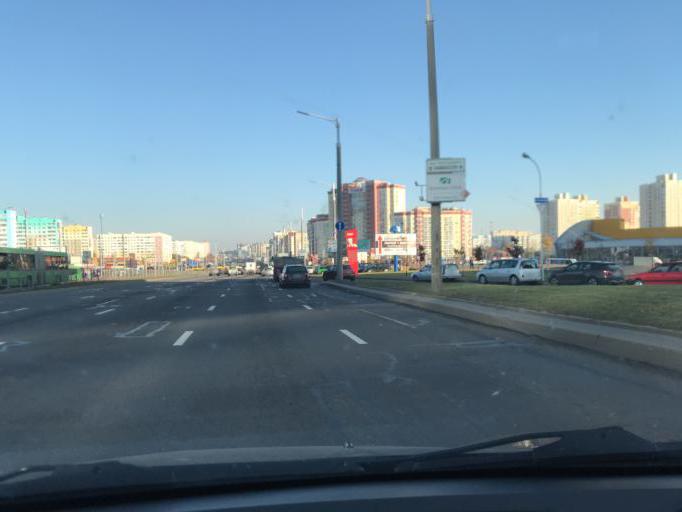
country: BY
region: Minsk
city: Novoye Medvezhino
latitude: 53.9071
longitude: 27.4317
